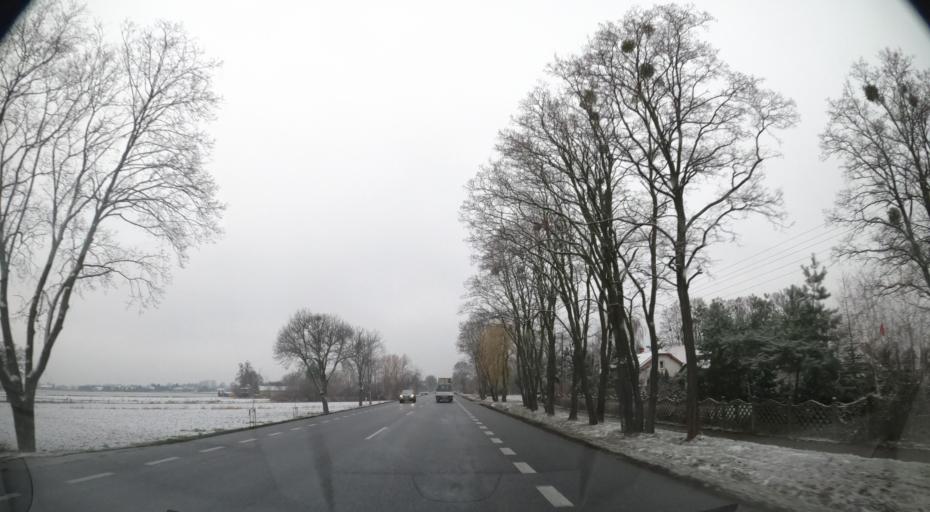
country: PL
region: Masovian Voivodeship
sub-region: Powiat sochaczewski
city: Paprotnia
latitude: 52.2072
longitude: 20.4817
